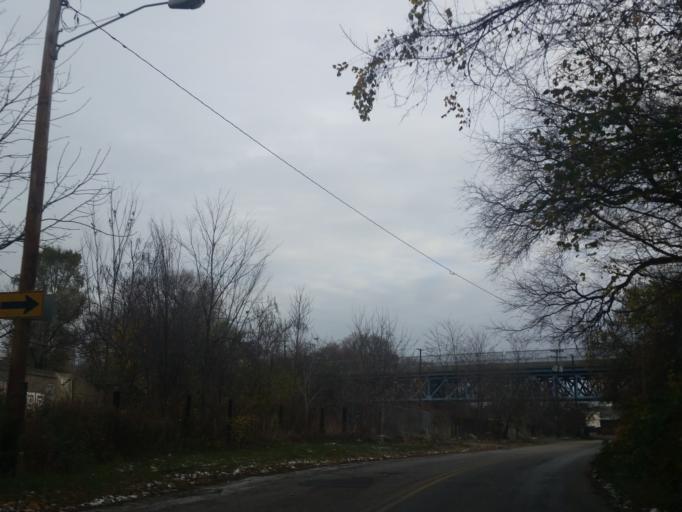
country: US
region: Ohio
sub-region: Cuyahoga County
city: Cleveland
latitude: 41.4788
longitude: -81.7017
